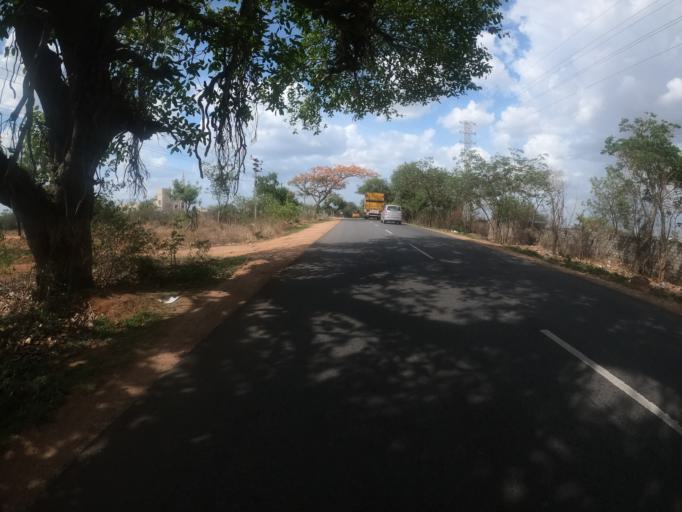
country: IN
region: Telangana
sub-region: Rangareddi
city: Sriramnagar
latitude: 17.3217
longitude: 78.2649
